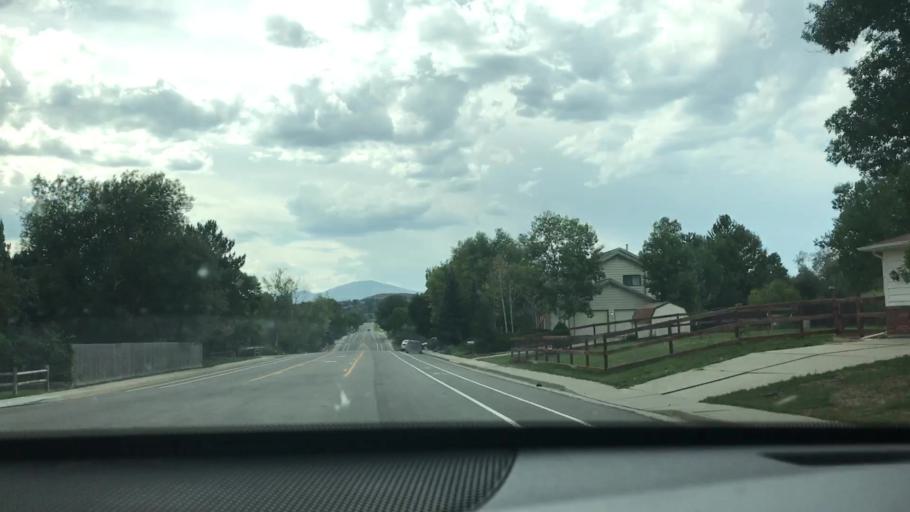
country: US
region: Colorado
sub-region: Larimer County
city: Loveland
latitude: 40.4147
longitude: -105.1161
